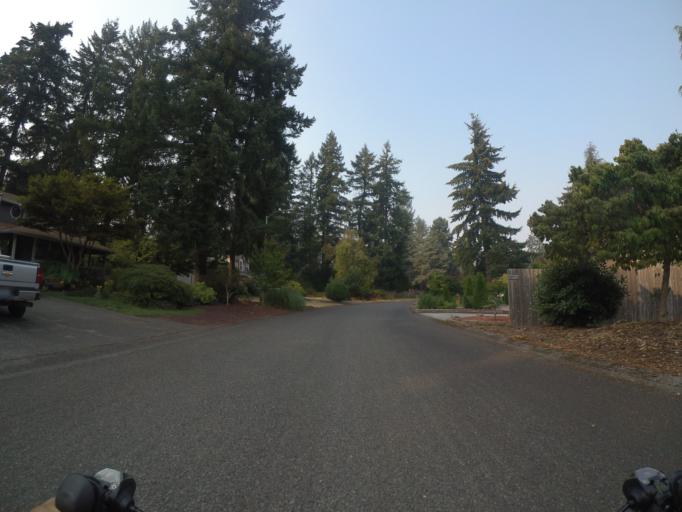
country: US
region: Washington
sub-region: Pierce County
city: Lakewood
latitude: 47.1433
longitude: -122.5205
